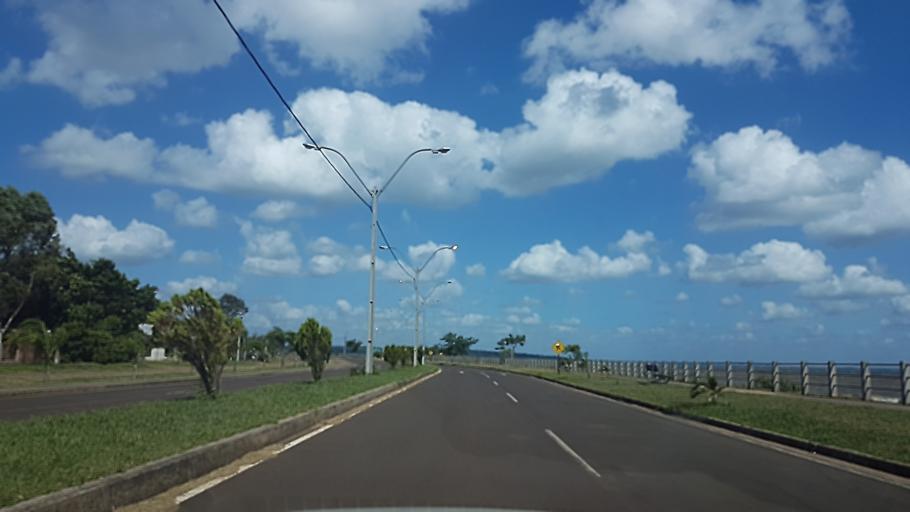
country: PY
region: Itapua
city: Carmen del Parana
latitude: -27.2274
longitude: -56.1593
